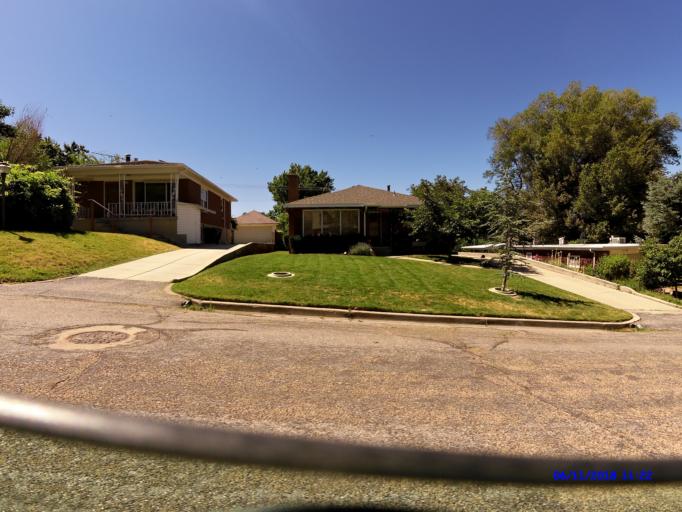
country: US
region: Utah
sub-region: Weber County
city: Ogden
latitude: 41.2234
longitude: -111.9386
